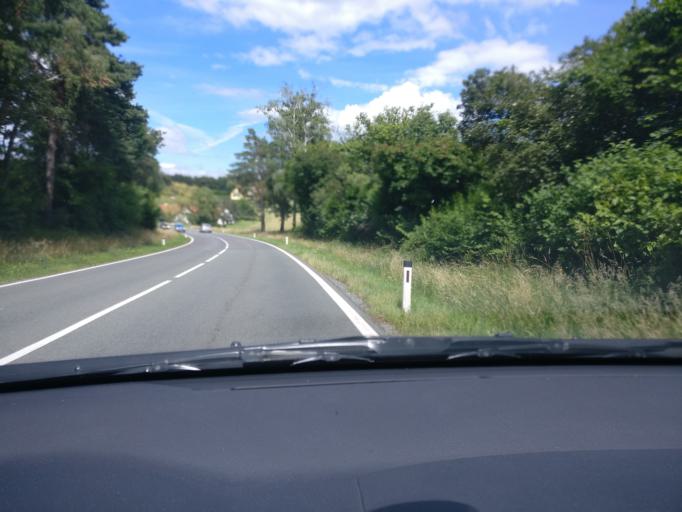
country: AT
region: Styria
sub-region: Politischer Bezirk Hartberg-Fuerstenfeld
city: Kaibing
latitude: 47.2060
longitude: 15.8518
